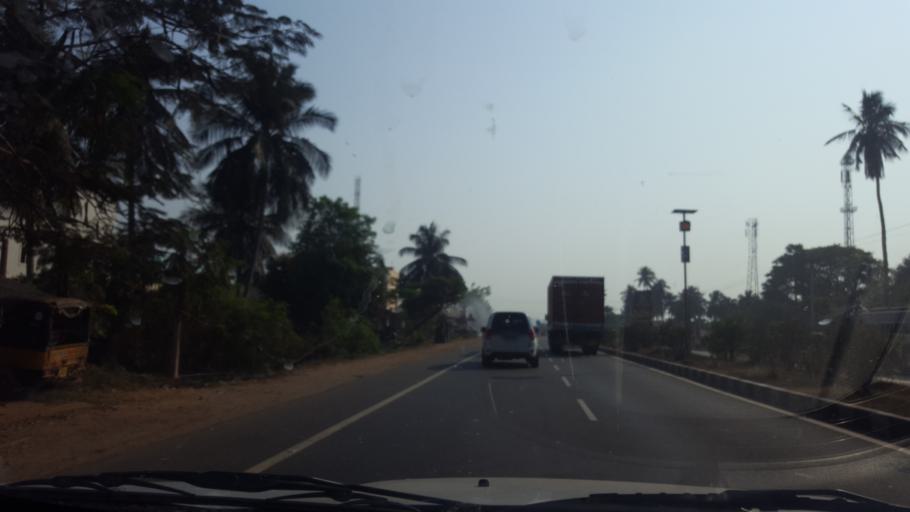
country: IN
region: Andhra Pradesh
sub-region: Vishakhapatnam
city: Elamanchili
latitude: 17.5964
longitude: 82.8727
